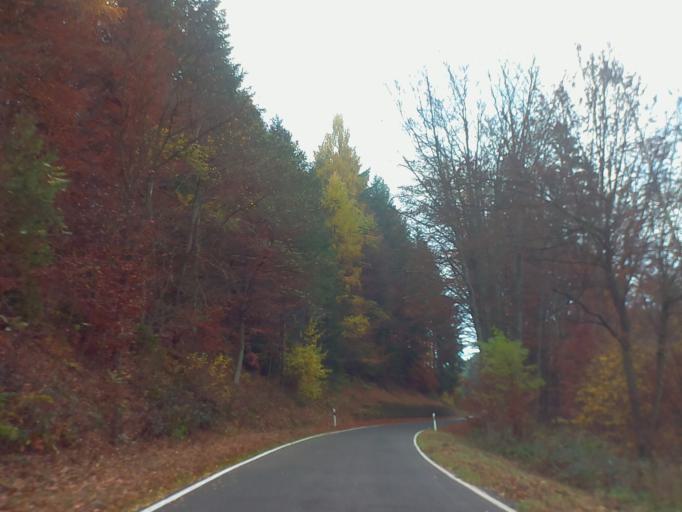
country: DE
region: Rheinland-Pfalz
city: Altleiningen
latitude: 49.4838
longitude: 8.0760
